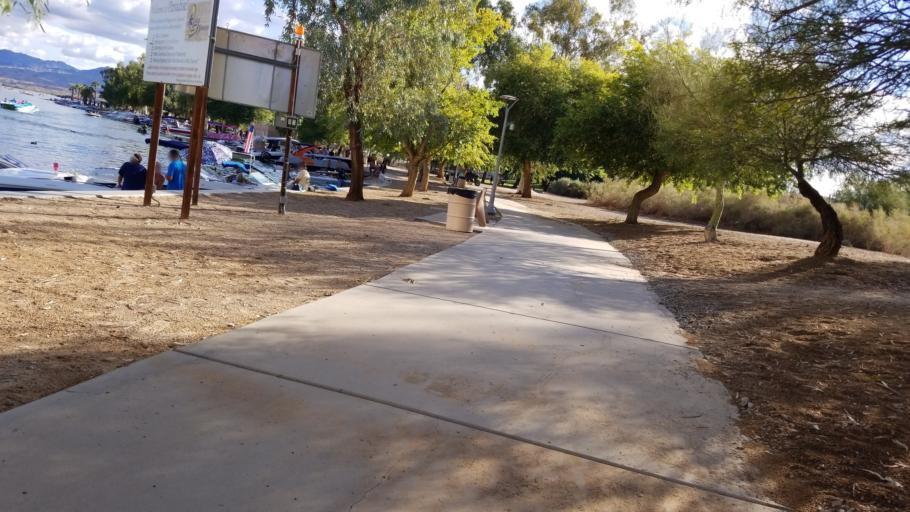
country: US
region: Arizona
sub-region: Mohave County
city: Lake Havasu City
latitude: 34.4690
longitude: -114.3481
